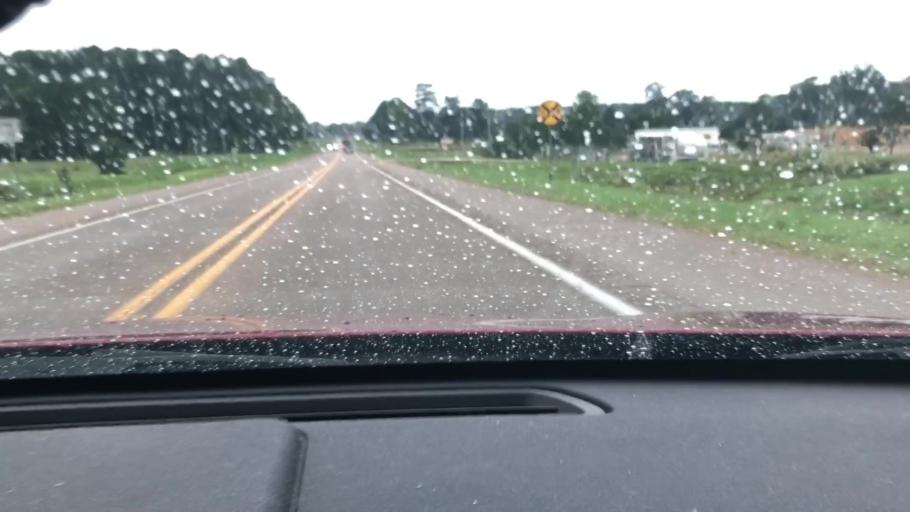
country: US
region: Arkansas
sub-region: Columbia County
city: Magnolia
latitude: 33.2972
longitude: -93.2401
